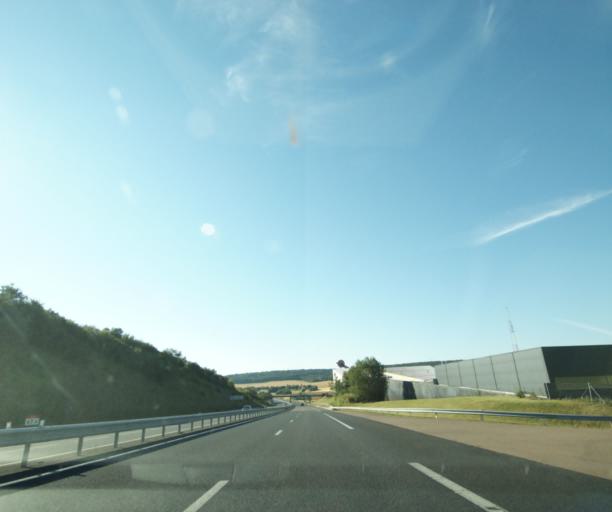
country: FR
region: Bourgogne
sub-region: Departement de l'Yonne
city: Soucy
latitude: 48.2526
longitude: 3.3383
